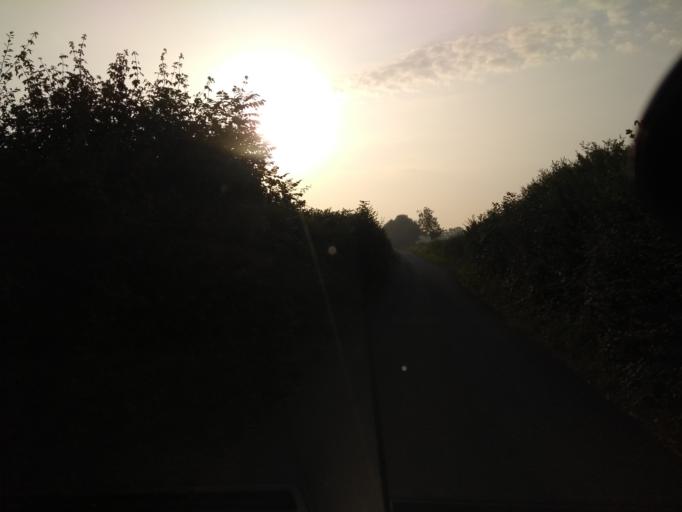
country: GB
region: England
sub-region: Somerset
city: Ilminster
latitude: 50.9882
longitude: -2.9365
